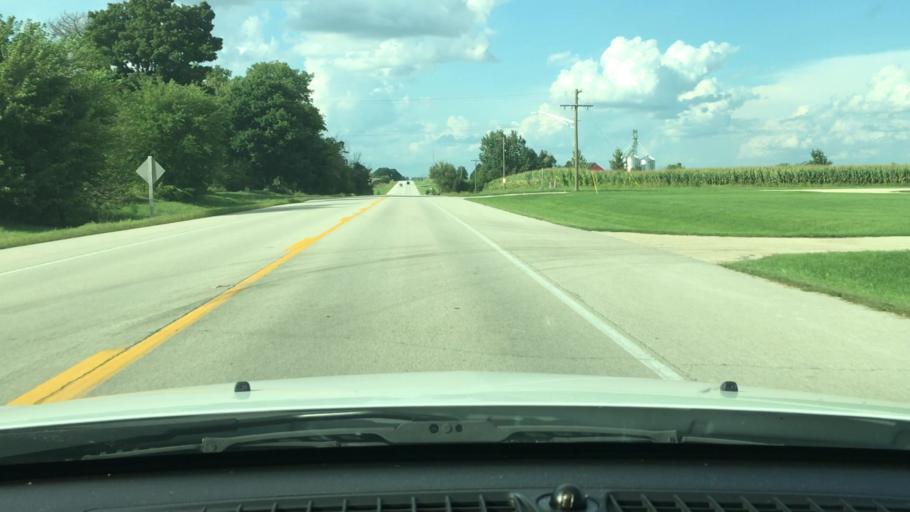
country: US
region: Illinois
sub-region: DeKalb County
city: Waterman
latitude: 41.7752
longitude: -88.7542
